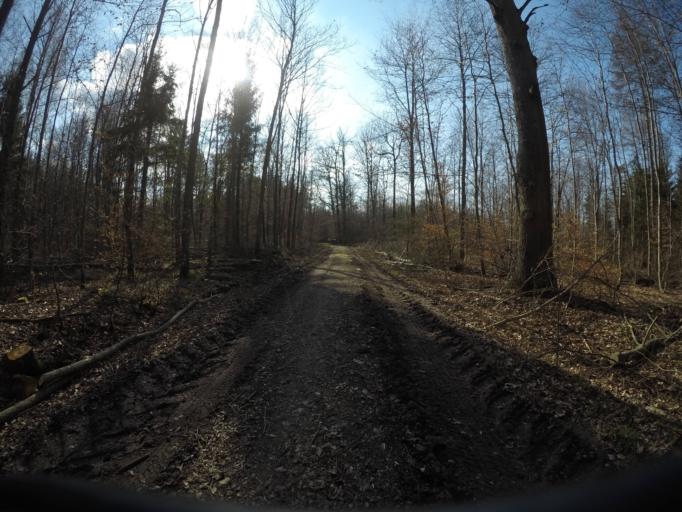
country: DE
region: Baden-Wuerttemberg
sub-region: Tuebingen Region
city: Dusslingen
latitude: 48.4616
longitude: 9.0231
